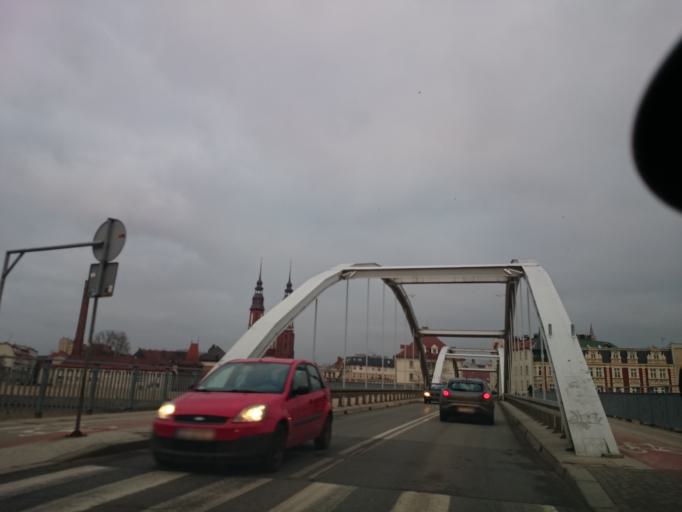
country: PL
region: Opole Voivodeship
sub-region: Powiat opolski
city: Opole
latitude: 50.6693
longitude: 17.9161
